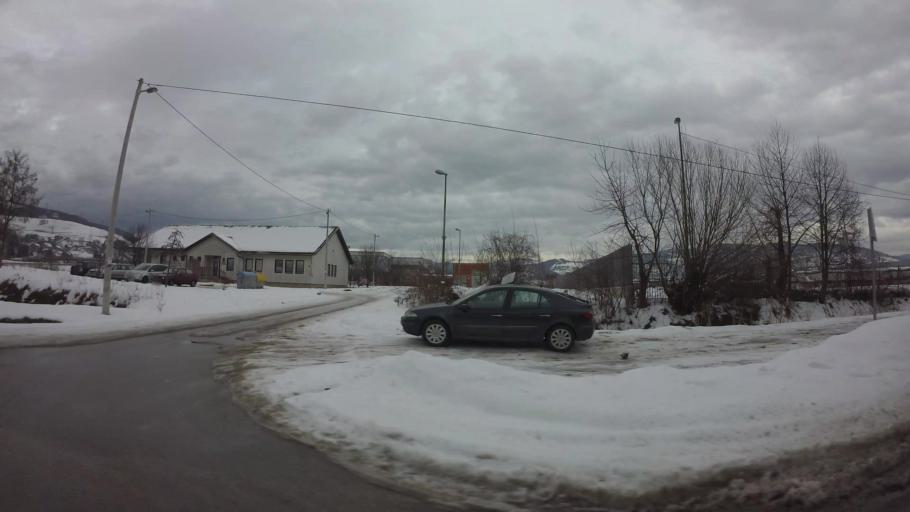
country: BA
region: Federation of Bosnia and Herzegovina
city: Vogosca
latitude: 43.8805
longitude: 18.3057
